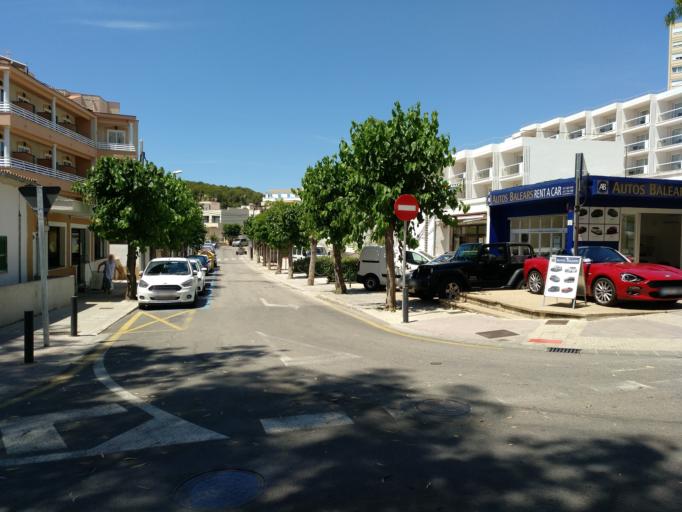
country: ES
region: Balearic Islands
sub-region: Illes Balears
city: Camp de Mar
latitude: 39.5383
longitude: 2.4481
